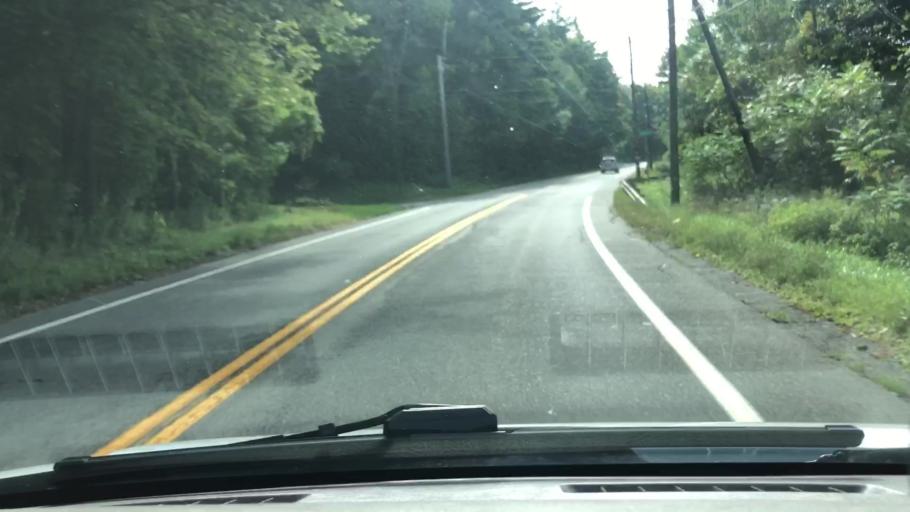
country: US
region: Massachusetts
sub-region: Berkshire County
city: North Adams
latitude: 42.6945
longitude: -73.0874
